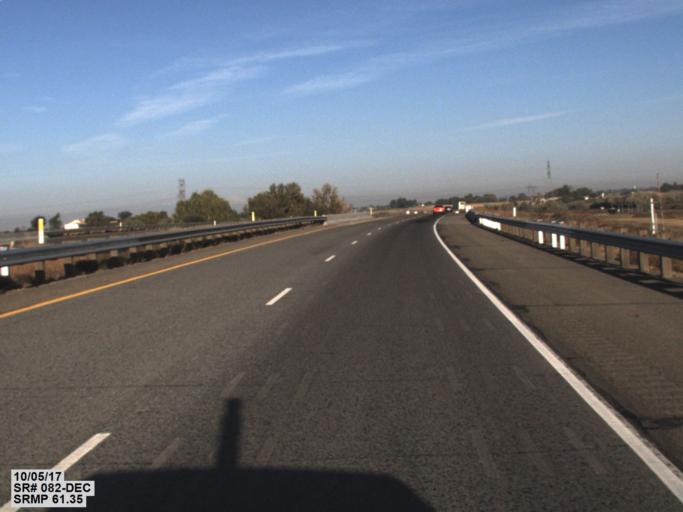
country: US
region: Washington
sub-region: Yakima County
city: Granger
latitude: 46.3334
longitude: -120.1243
